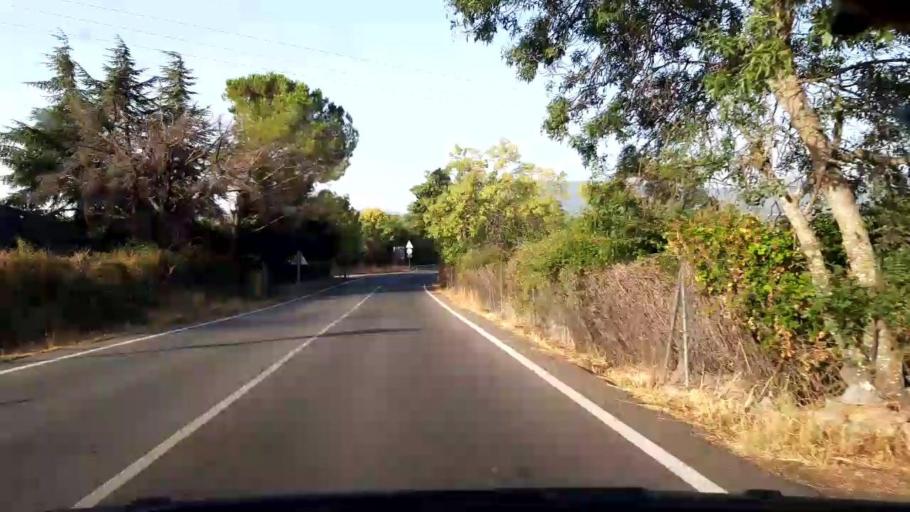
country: ES
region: Madrid
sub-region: Provincia de Madrid
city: Collado Mediano
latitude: 40.6913
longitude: -4.0487
